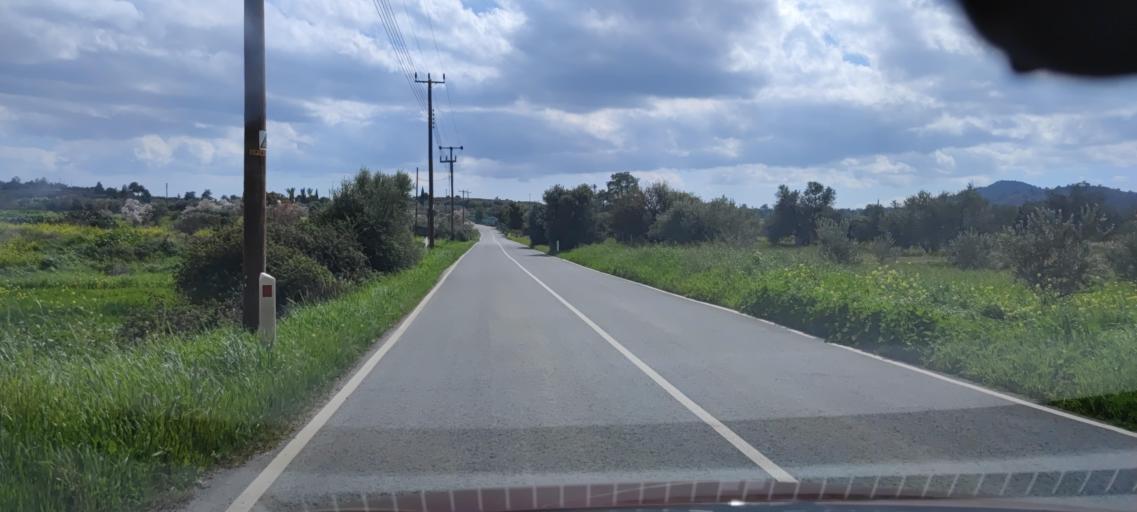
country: CY
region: Lefkosia
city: Lythrodontas
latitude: 34.9915
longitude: 33.2962
